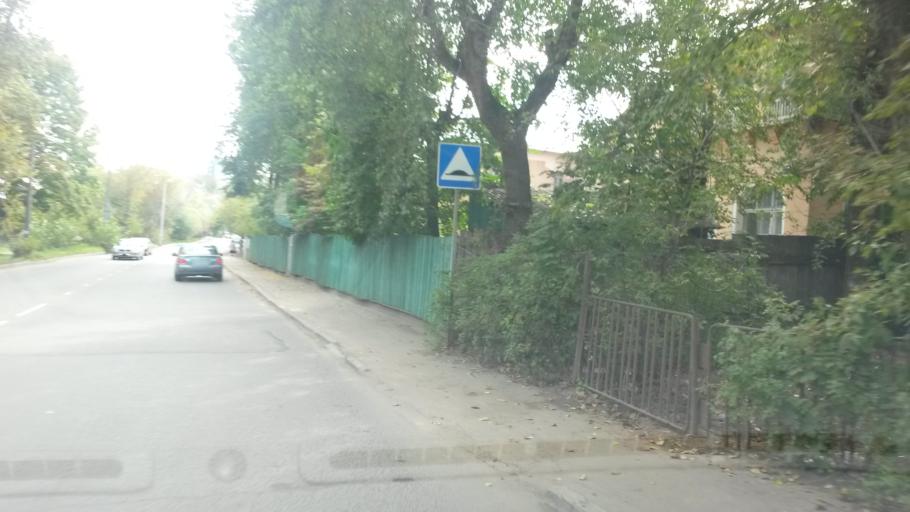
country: RU
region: Ivanovo
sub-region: Gorod Ivanovo
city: Ivanovo
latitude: 57.0083
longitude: 40.9578
